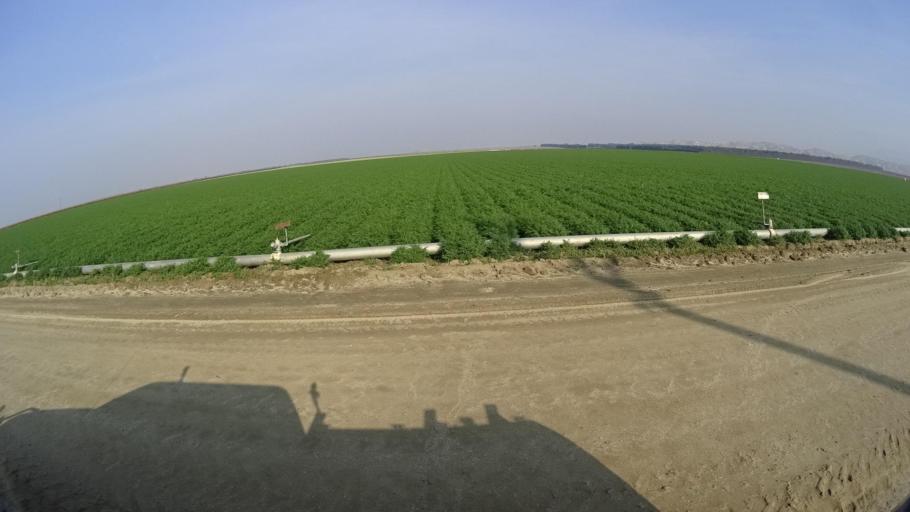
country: US
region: California
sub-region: Kern County
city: Arvin
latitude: 35.0928
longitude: -118.8559
